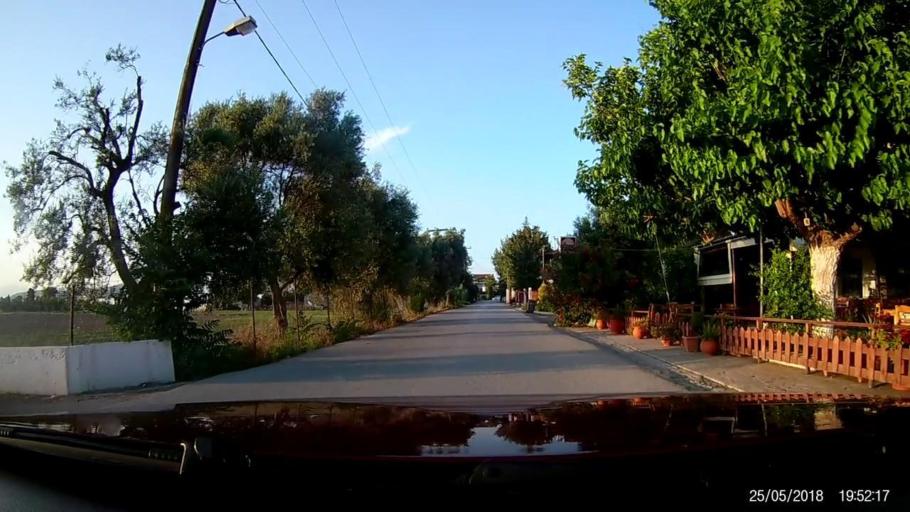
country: GR
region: Central Greece
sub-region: Nomos Evvoias
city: Ayios Nikolaos
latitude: 38.4101
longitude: 23.6445
